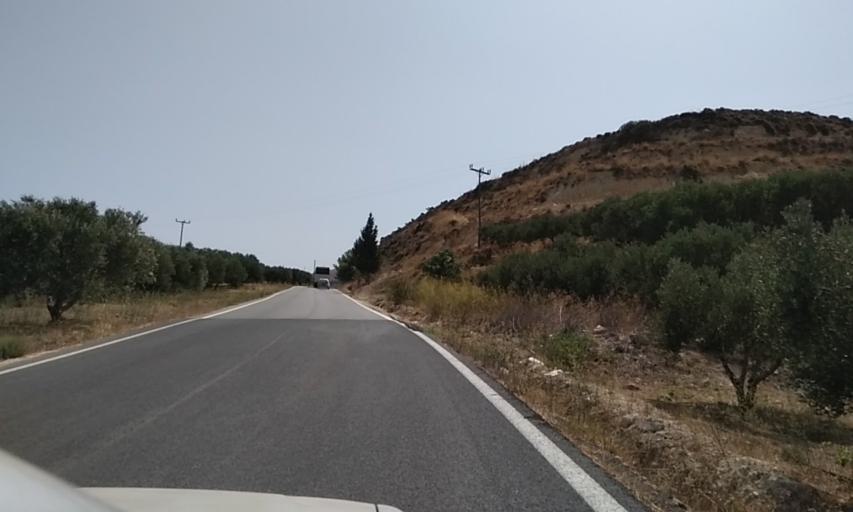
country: GR
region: Crete
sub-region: Nomos Lasithiou
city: Siteia
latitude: 35.1089
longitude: 26.0573
